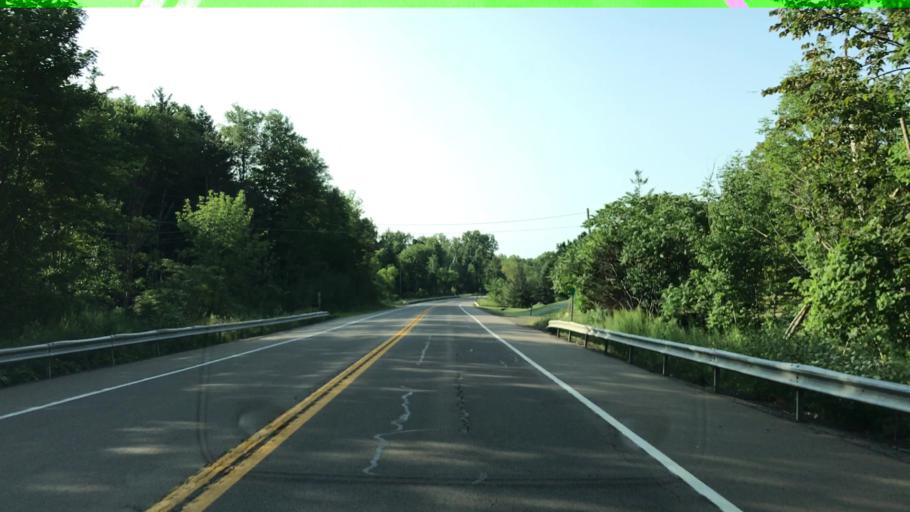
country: US
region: New York
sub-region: Chautauqua County
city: Fredonia
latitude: 42.3656
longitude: -79.3126
